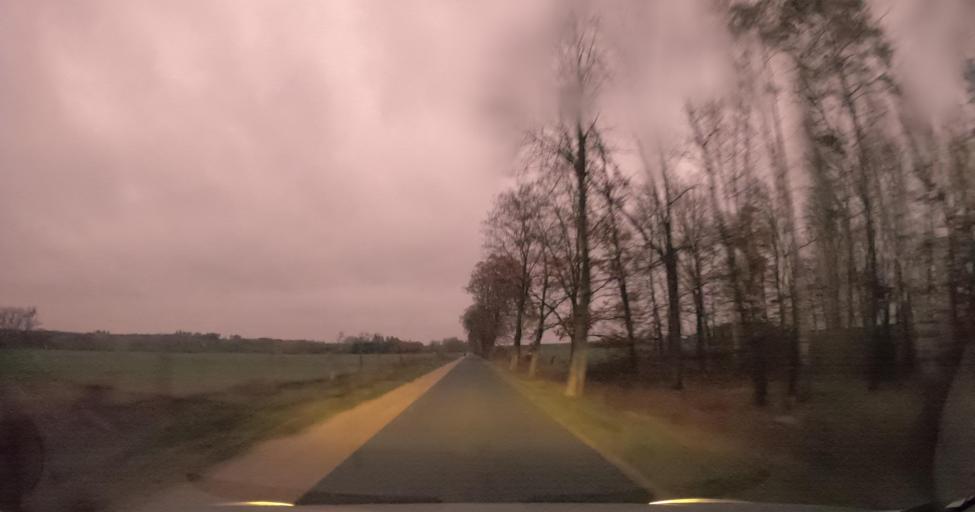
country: PL
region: West Pomeranian Voivodeship
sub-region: Powiat bialogardzki
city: Tychowo
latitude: 53.8821
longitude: 16.2340
